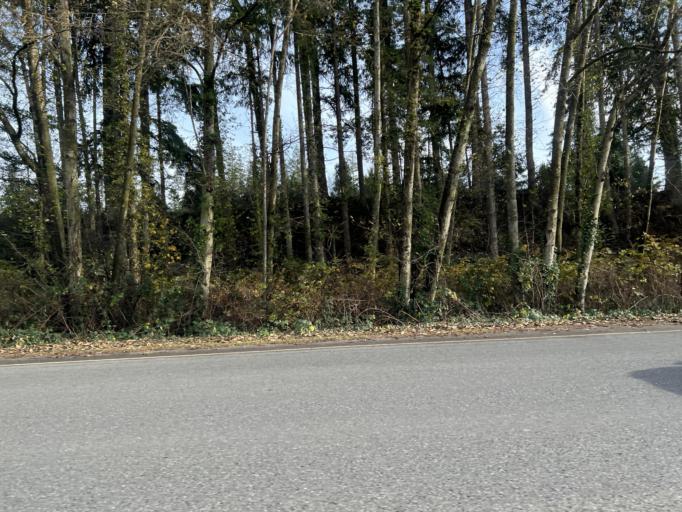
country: US
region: Washington
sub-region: Kitsap County
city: Bainbridge Island
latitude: 47.6373
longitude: -122.5129
